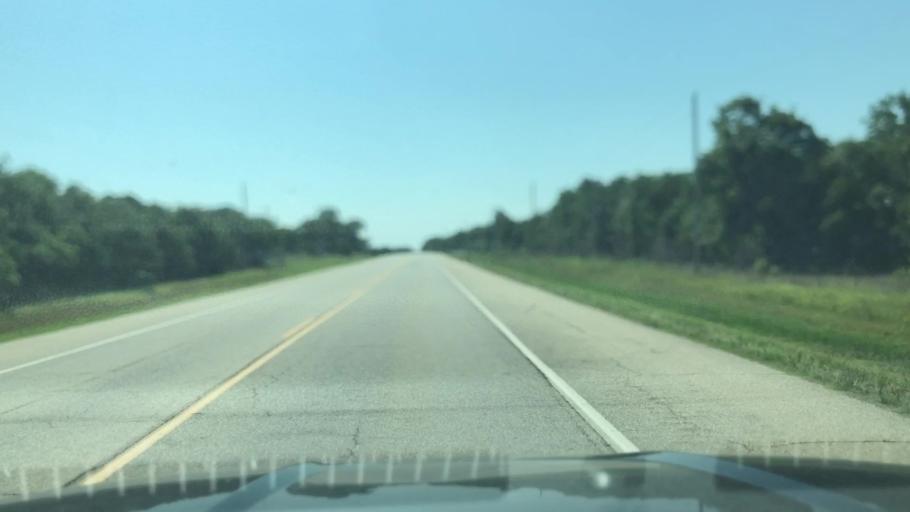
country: US
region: Oklahoma
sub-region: Creek County
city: Mannford
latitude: 35.9930
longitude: -96.3550
